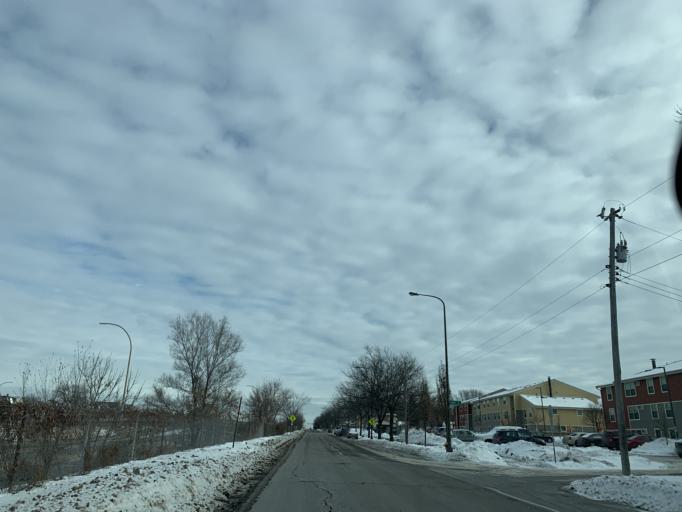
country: US
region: Minnesota
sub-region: Ramsey County
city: Saint Paul
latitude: 44.9512
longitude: -93.1336
